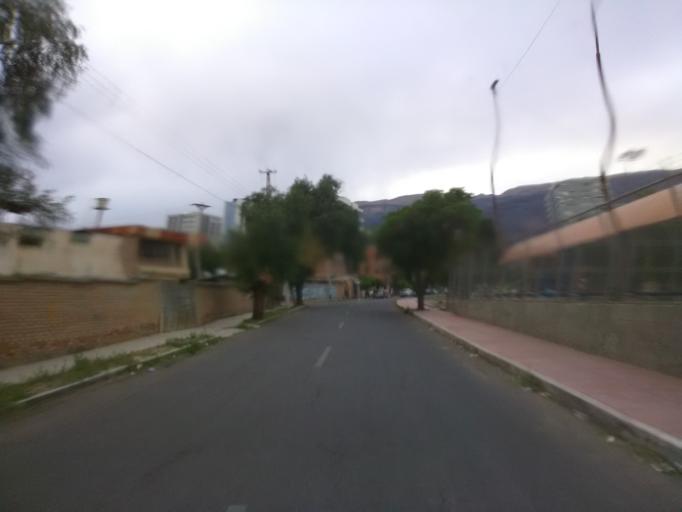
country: BO
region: Cochabamba
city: Cochabamba
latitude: -17.3762
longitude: -66.1457
